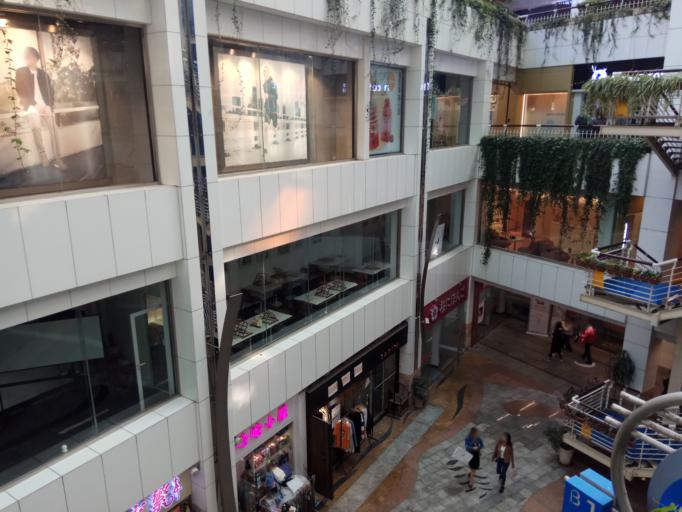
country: CN
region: Shanghai Shi
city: Changning
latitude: 31.2210
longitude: 121.4143
